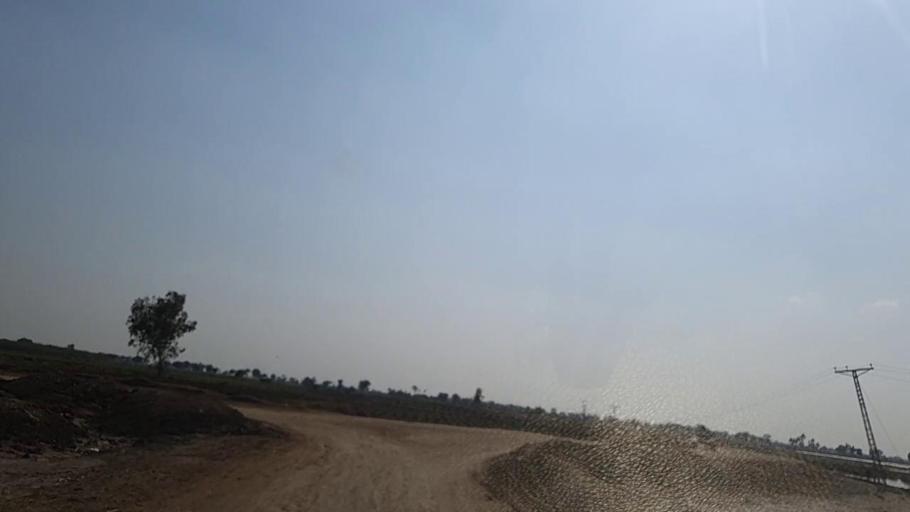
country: PK
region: Sindh
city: Daur
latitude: 26.4582
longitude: 68.2505
